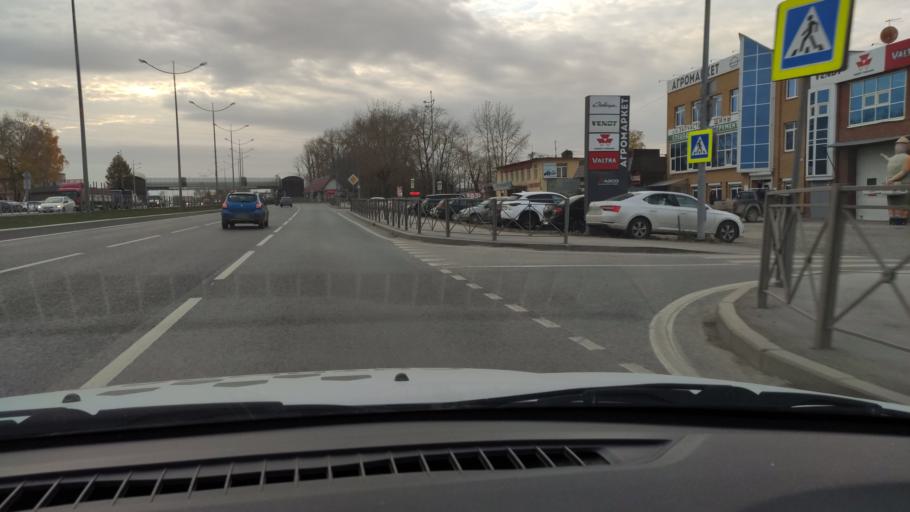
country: RU
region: Perm
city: Kondratovo
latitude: 57.9543
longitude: 56.1153
